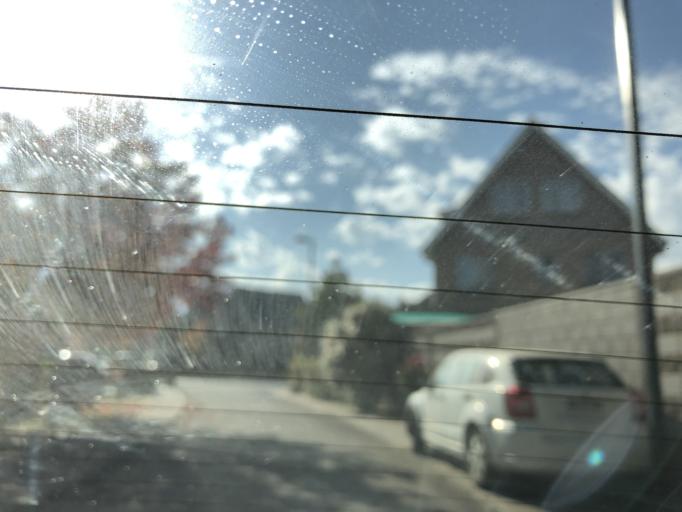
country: CL
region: Santiago Metropolitan
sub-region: Provincia de Cordillera
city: Puente Alto
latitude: -33.6026
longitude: -70.5150
